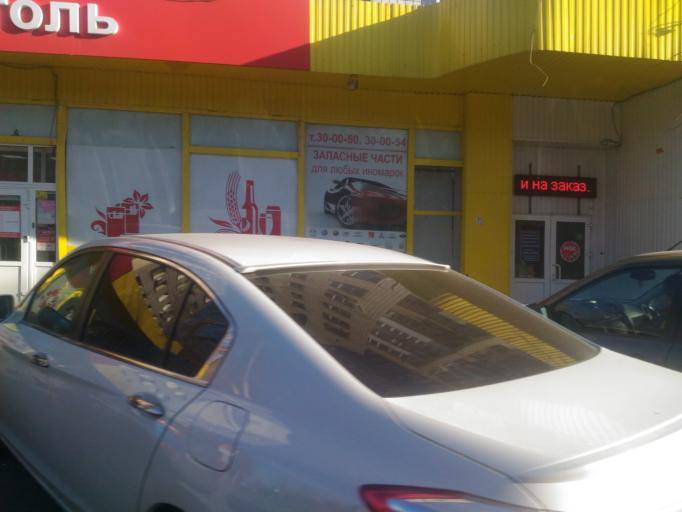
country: RU
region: Ulyanovsk
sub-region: Ulyanovskiy Rayon
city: Ulyanovsk
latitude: 54.3079
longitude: 48.3791
